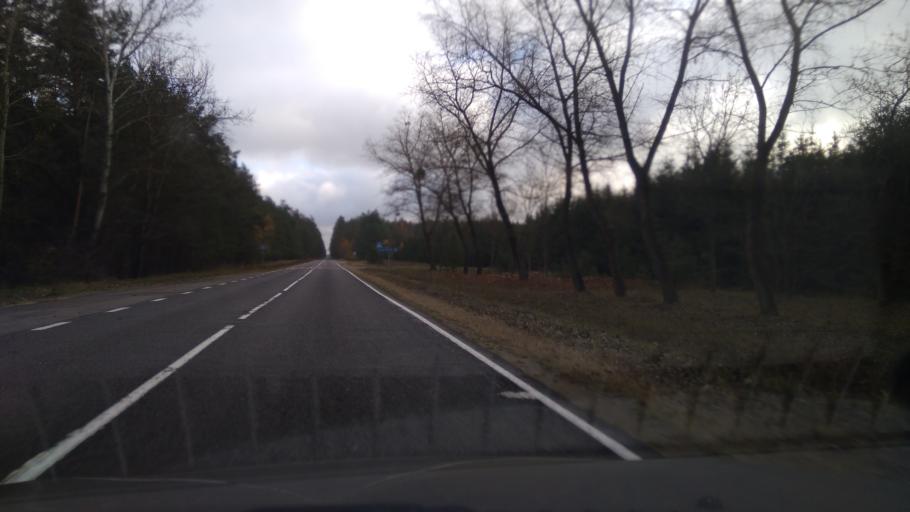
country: BY
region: Minsk
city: Slutsk
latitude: 53.2311
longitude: 27.6692
